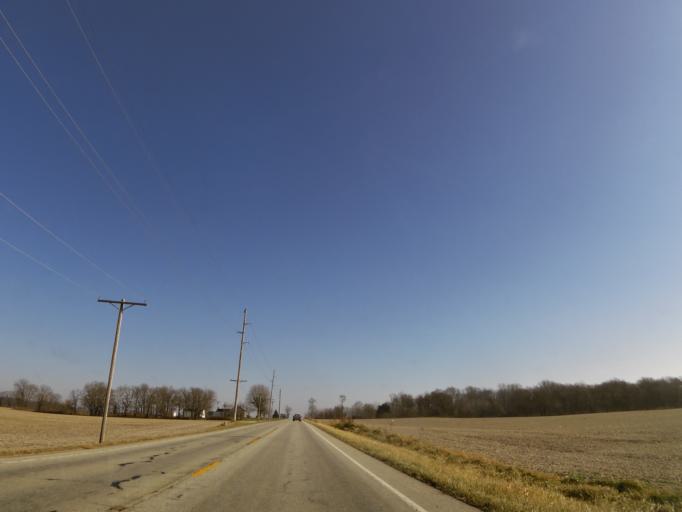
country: US
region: Indiana
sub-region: Fayette County
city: Connersville
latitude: 39.6269
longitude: -85.2757
